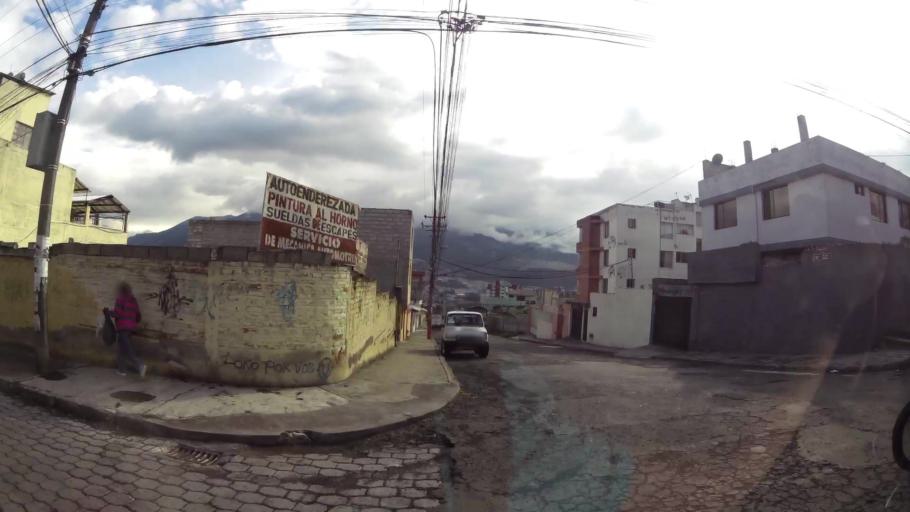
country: EC
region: Pichincha
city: Quito
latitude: -0.1322
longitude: -78.4721
